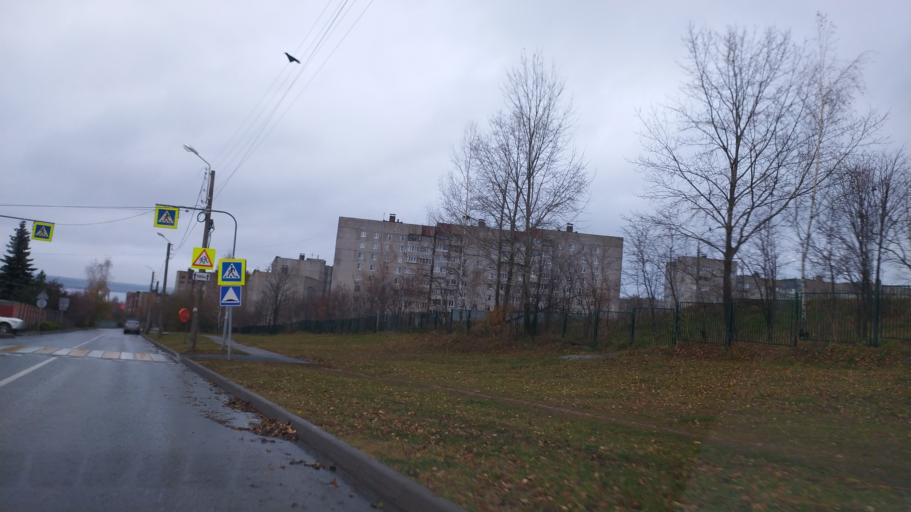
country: RU
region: Chuvashia
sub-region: Cheboksarskiy Rayon
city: Cheboksary
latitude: 56.1456
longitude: 47.1618
